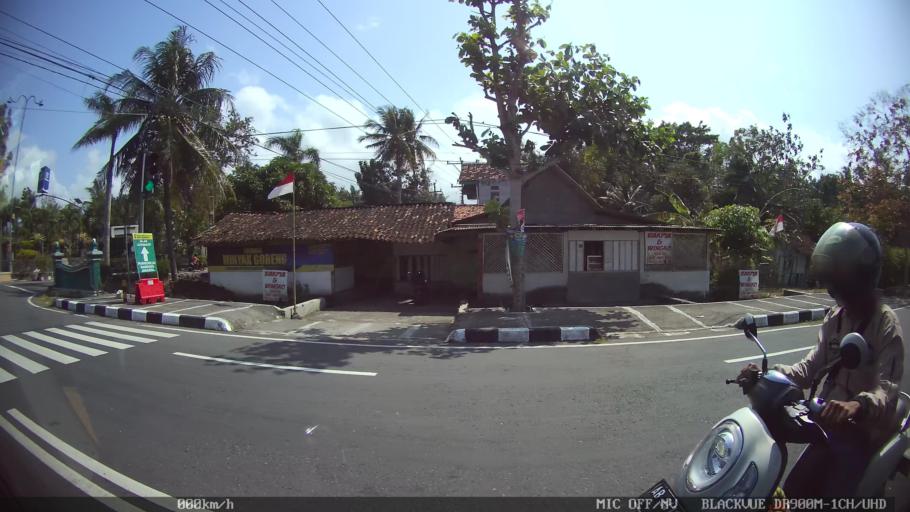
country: ID
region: Daerah Istimewa Yogyakarta
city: Srandakan
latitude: -7.8921
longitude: 110.1293
